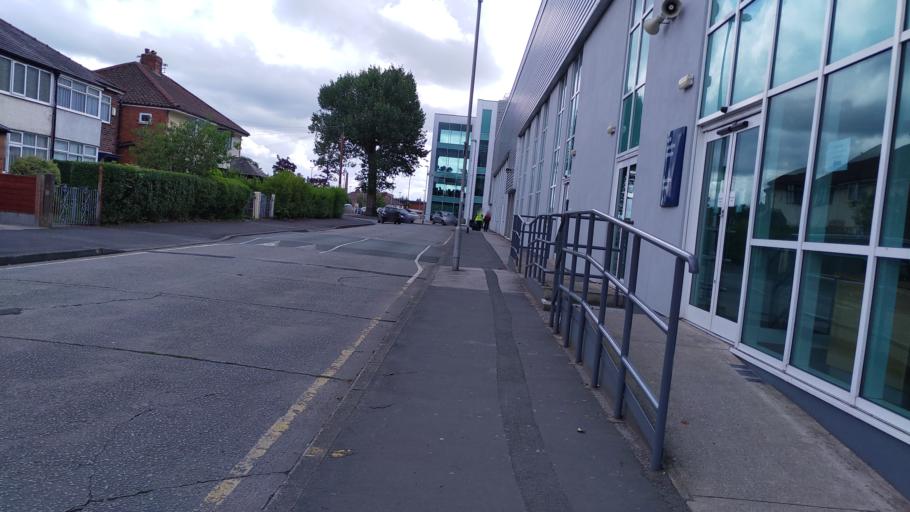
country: GB
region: England
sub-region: Lancashire
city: Preston
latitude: 53.7727
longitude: -2.6873
